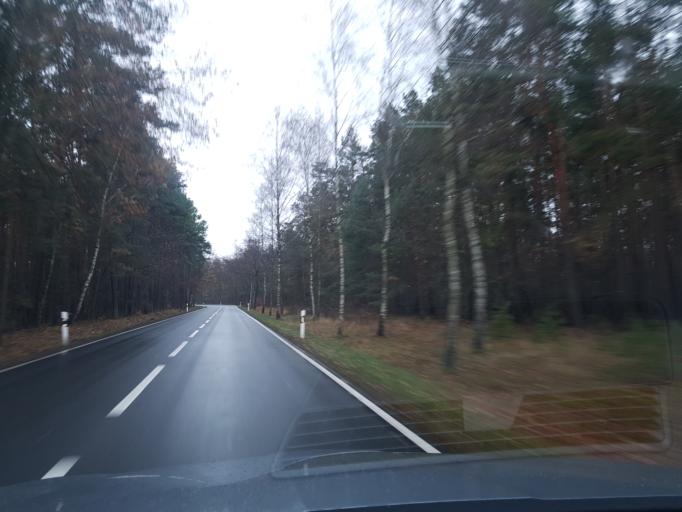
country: DE
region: Brandenburg
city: Finsterwalde
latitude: 51.6531
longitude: 13.6923
